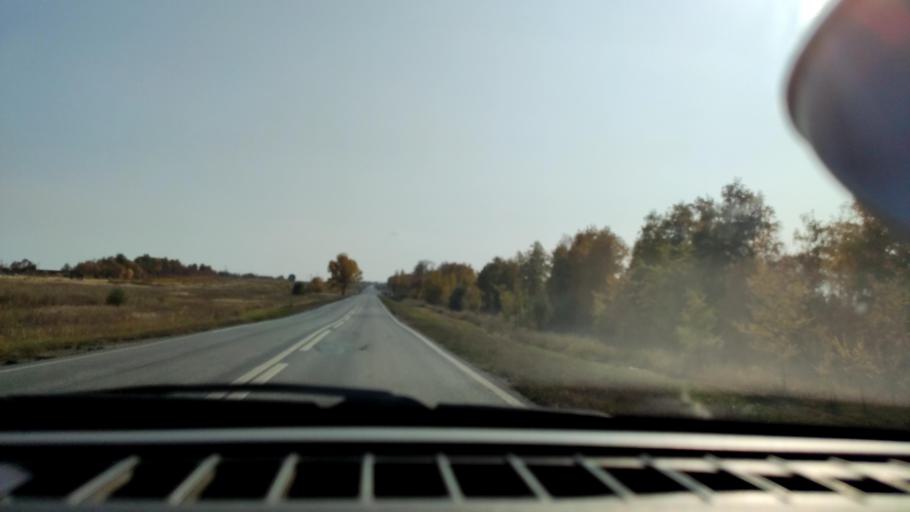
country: RU
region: Samara
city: Dubovyy Umet
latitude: 53.0981
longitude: 50.3498
